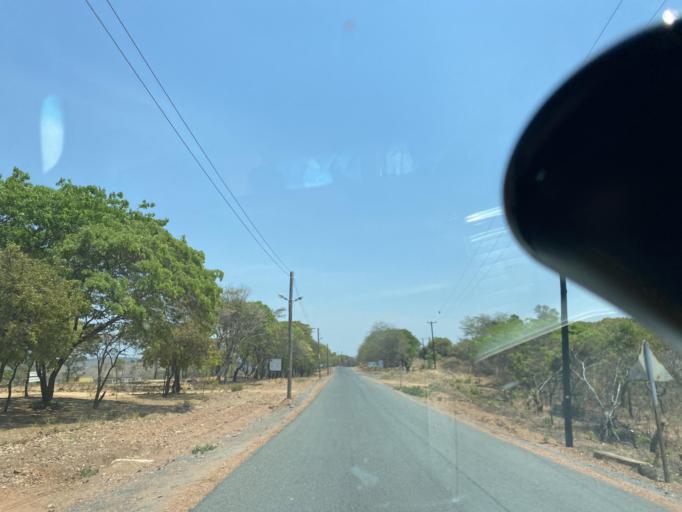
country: ZM
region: Lusaka
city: Kafue
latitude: -15.8661
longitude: 28.4484
